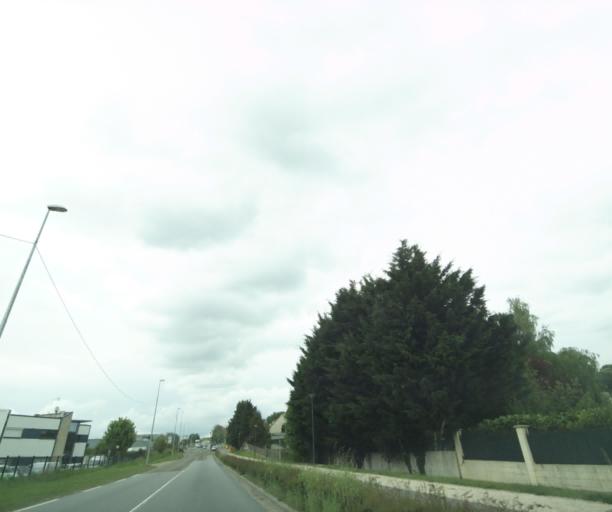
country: FR
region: Ile-de-France
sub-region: Departement des Yvelines
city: Ecquevilly
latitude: 48.9528
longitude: 1.9273
